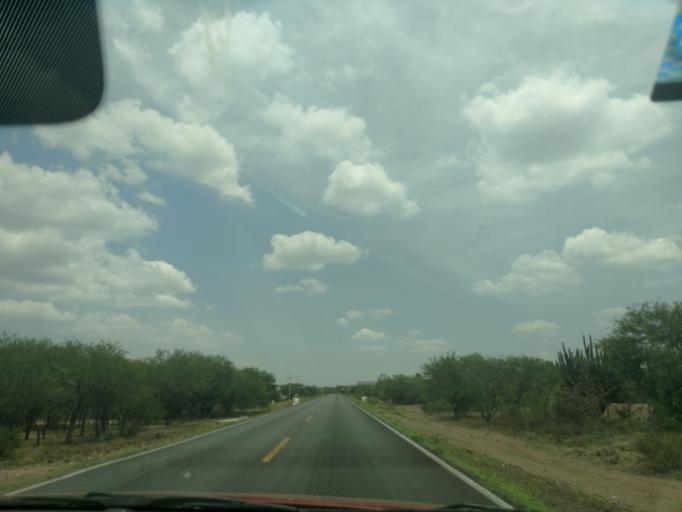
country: MX
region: San Luis Potosi
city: Villa Juarez
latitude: 22.0185
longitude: -100.3914
